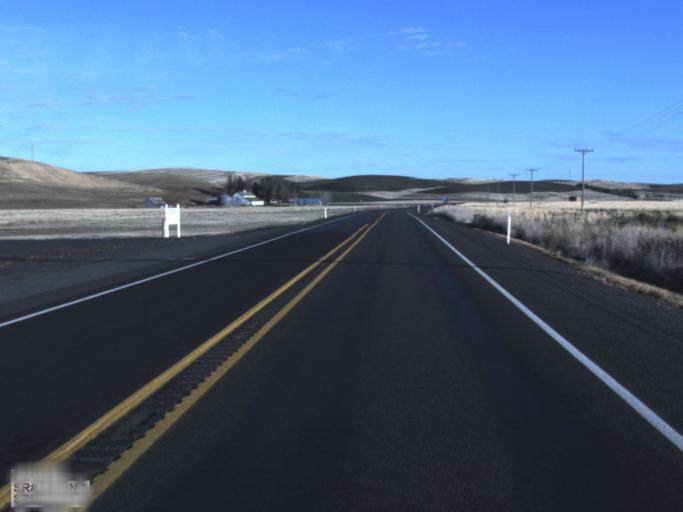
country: US
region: Washington
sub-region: Garfield County
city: Pomeroy
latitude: 46.7776
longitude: -117.7024
